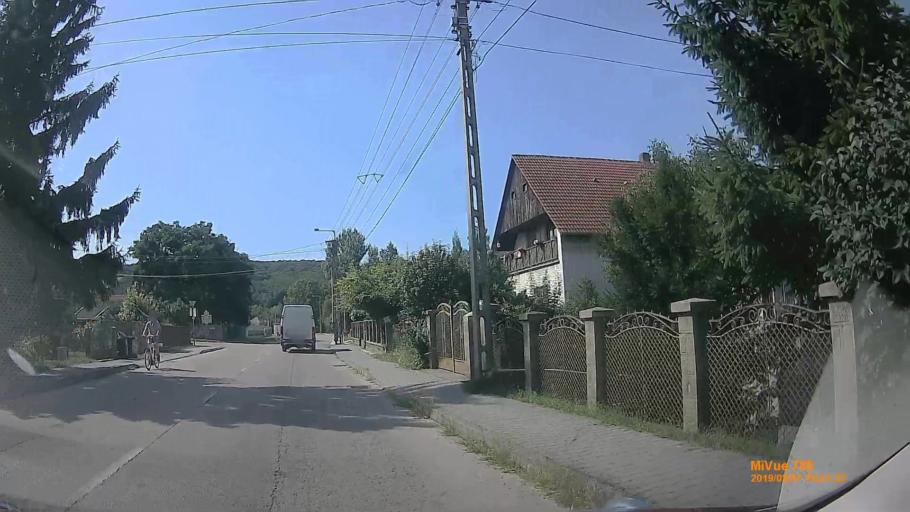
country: HU
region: Veszprem
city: Ajka
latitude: 47.0910
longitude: 17.5641
